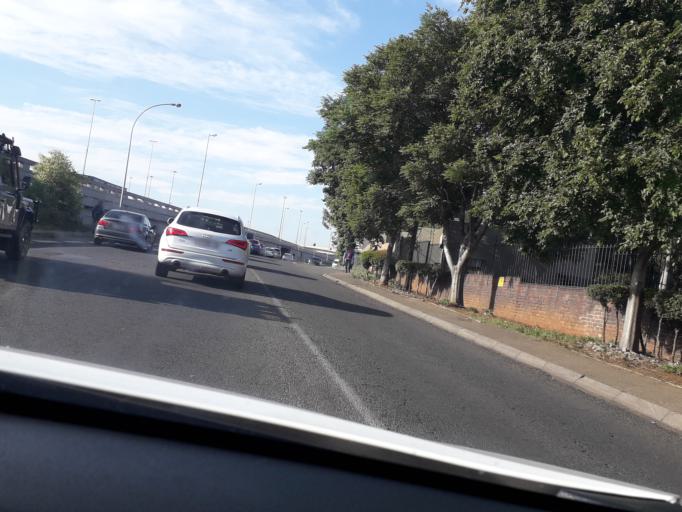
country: ZA
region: Gauteng
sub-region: City of Johannesburg Metropolitan Municipality
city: Modderfontein
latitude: -26.1639
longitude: 28.1329
